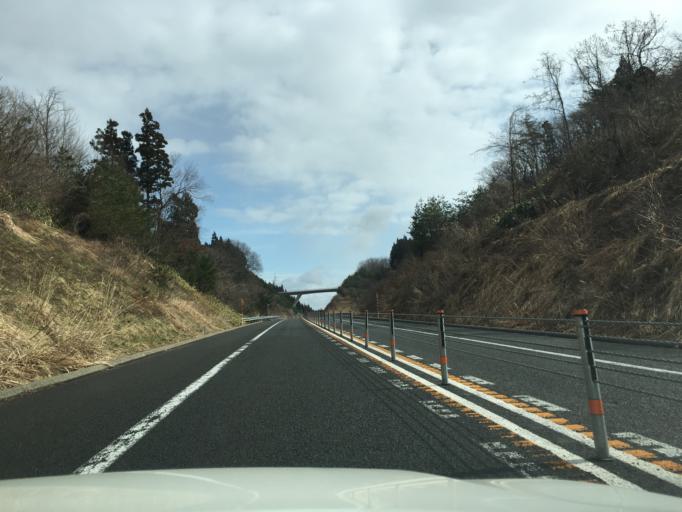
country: JP
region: Akita
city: Akita
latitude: 39.6299
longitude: 140.1645
